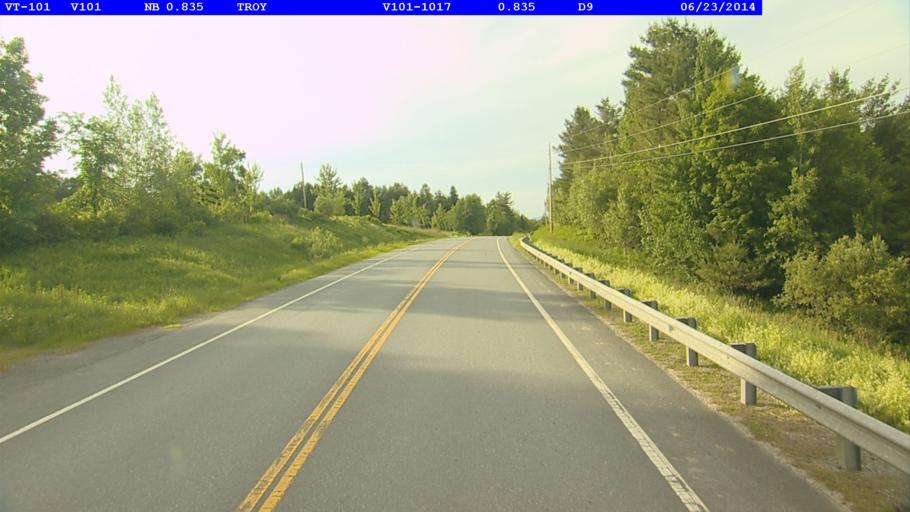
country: US
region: Vermont
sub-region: Orleans County
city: Newport
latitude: 44.9152
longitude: -72.4080
